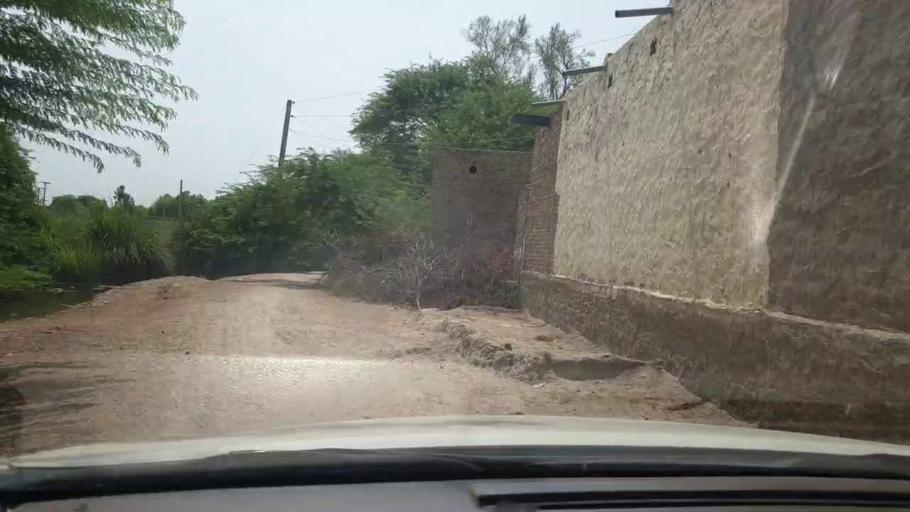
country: PK
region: Sindh
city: Shikarpur
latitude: 28.0191
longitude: 68.6481
